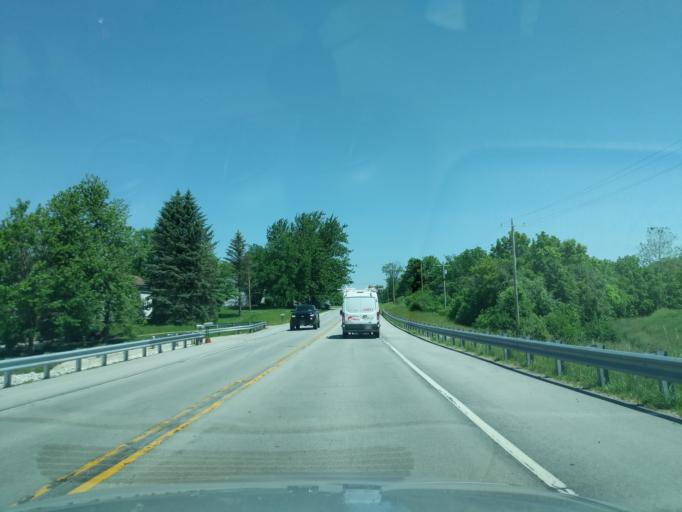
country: US
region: Indiana
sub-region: Whitley County
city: Columbia City
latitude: 41.1766
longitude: -85.4916
